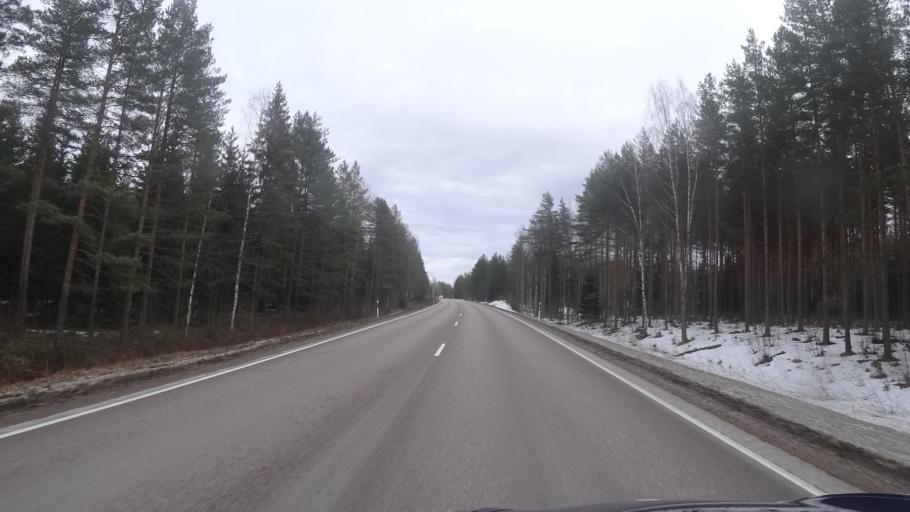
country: FI
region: Kymenlaakso
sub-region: Kouvola
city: Anjala
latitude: 60.6929
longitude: 26.6735
